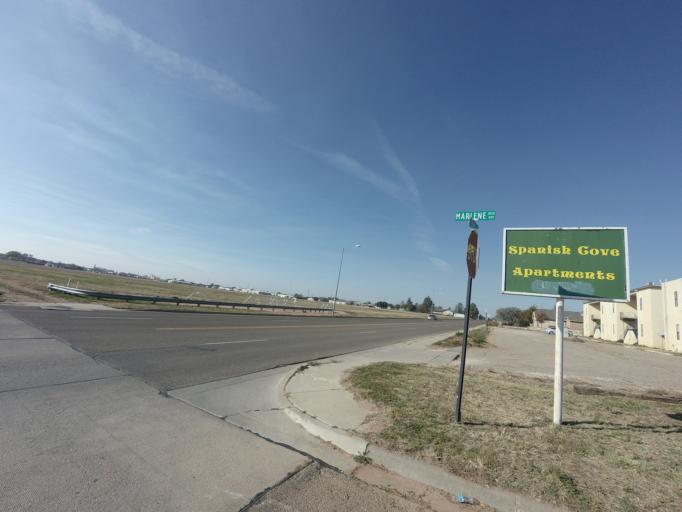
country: US
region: New Mexico
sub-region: Curry County
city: Clovis
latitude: 34.4050
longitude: -103.1752
